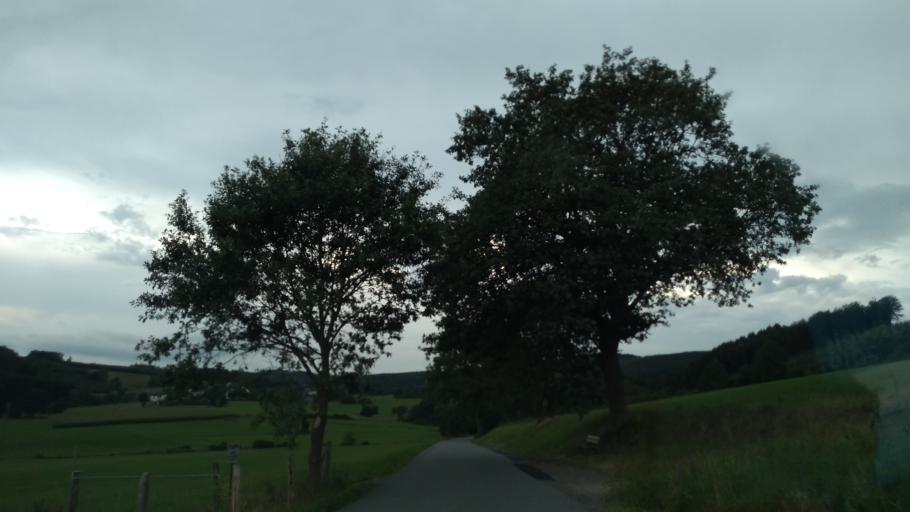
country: DE
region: North Rhine-Westphalia
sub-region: Regierungsbezirk Arnsberg
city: Herscheid
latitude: 51.1936
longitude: 7.7888
